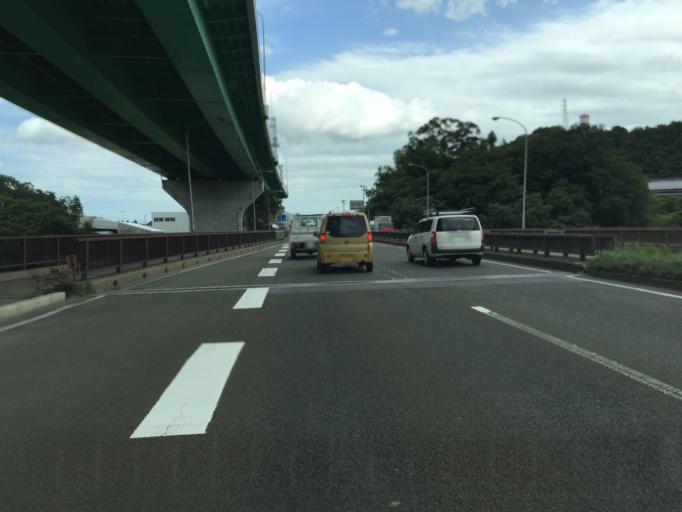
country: JP
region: Miyagi
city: Sendai
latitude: 38.2155
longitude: 140.8119
